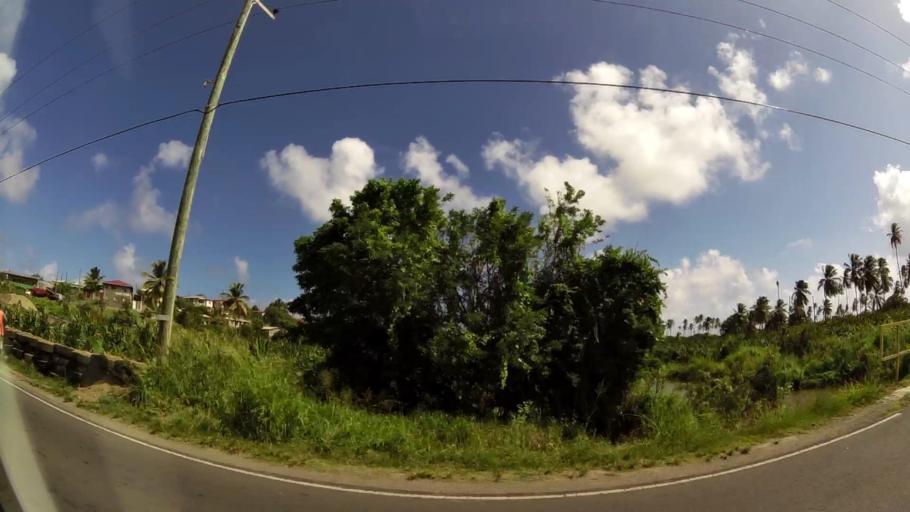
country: LC
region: Micoud Quarter
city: Micoud
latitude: 13.8165
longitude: -60.9012
